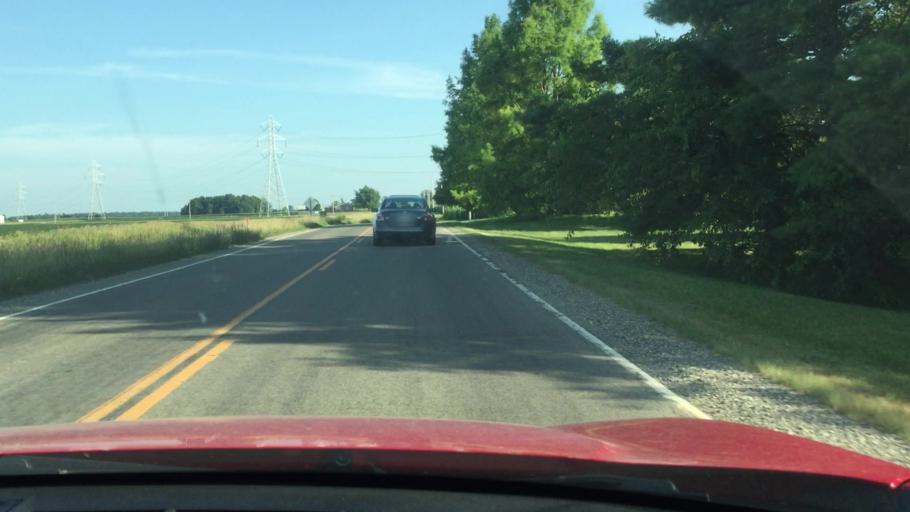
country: US
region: Ohio
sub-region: Hardin County
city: Ada
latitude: 40.6783
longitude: -83.8577
